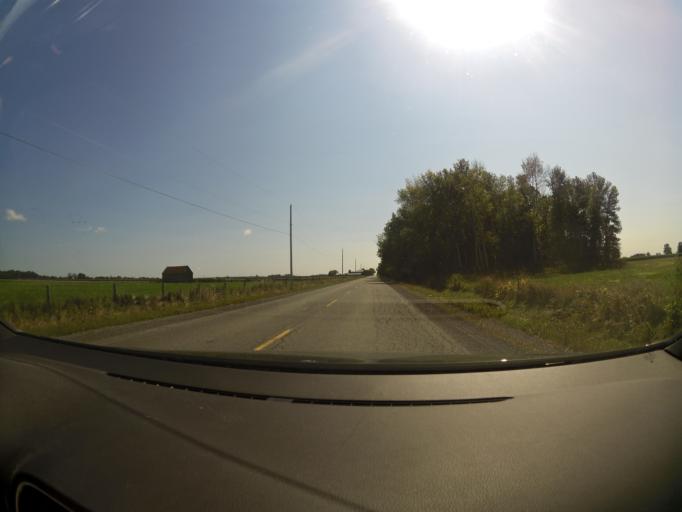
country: CA
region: Ontario
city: Arnprior
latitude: 45.3691
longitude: -76.2551
